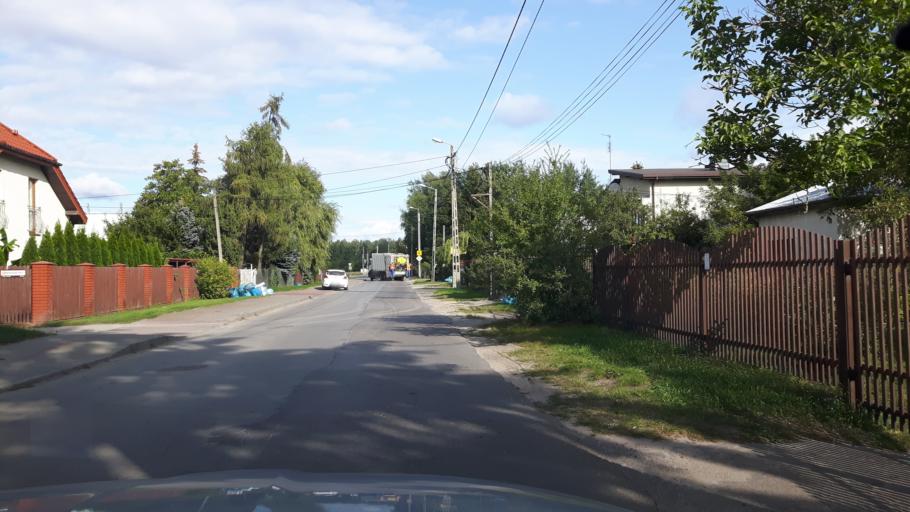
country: PL
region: Masovian Voivodeship
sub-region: Powiat wolominski
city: Marki
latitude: 52.3318
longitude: 21.0920
